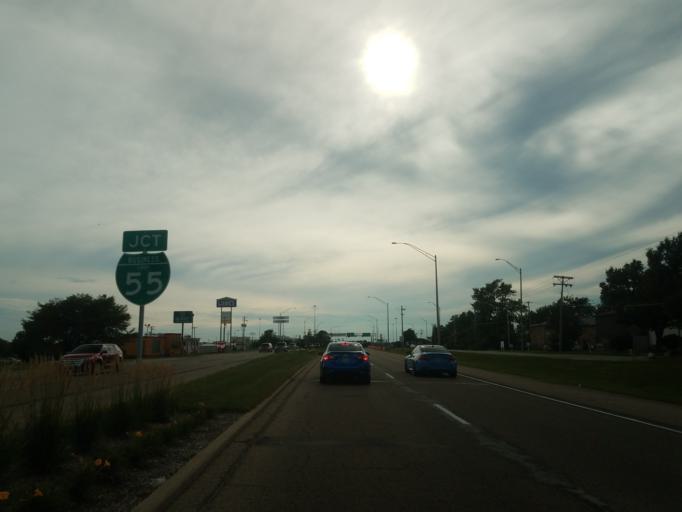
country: US
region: Illinois
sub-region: McLean County
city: Bloomington
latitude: 40.4884
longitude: -88.9464
